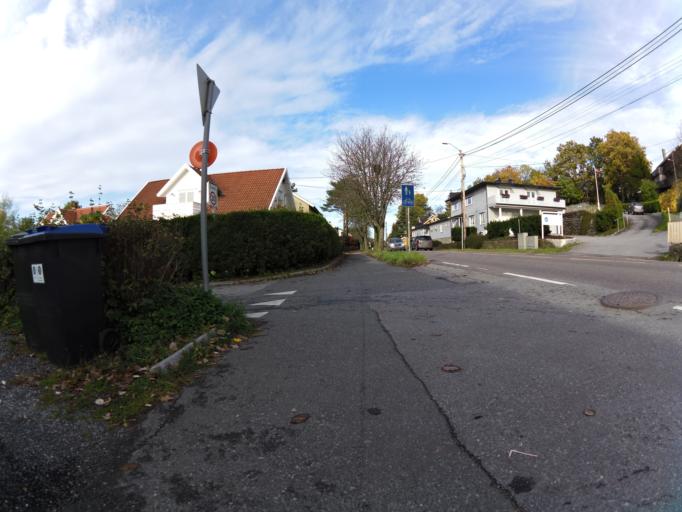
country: NO
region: Ostfold
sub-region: Fredrikstad
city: Fredrikstad
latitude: 59.2259
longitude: 10.9290
